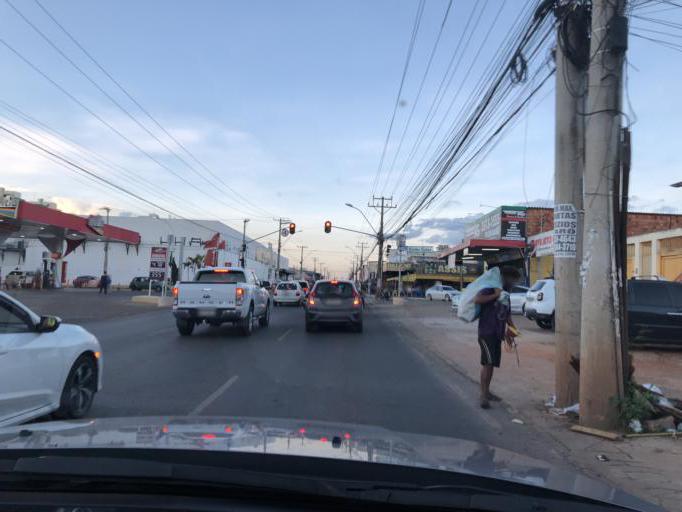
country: BR
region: Federal District
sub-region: Brasilia
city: Brasilia
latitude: -15.8094
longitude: -48.0690
